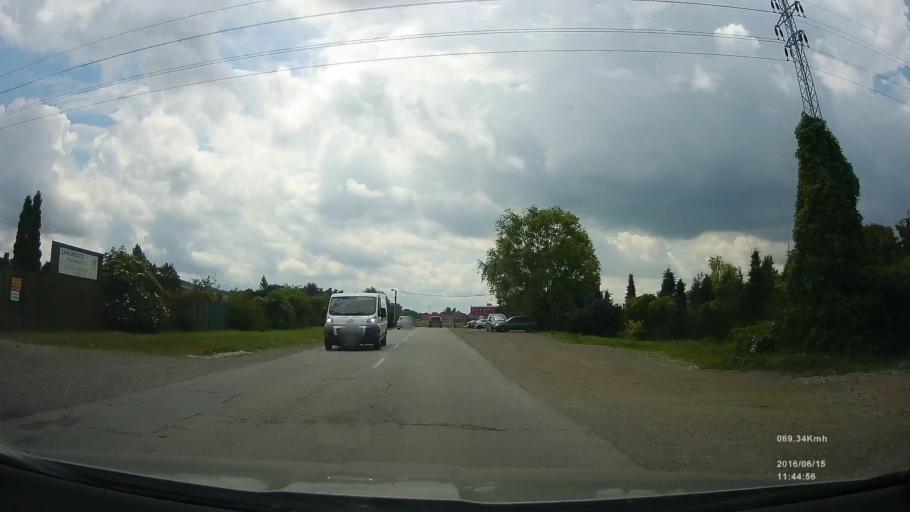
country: SK
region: Kosicky
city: Kosice
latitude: 48.7396
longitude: 21.3460
